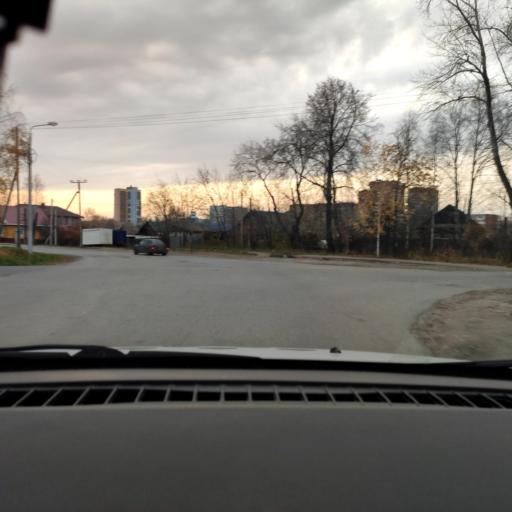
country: RU
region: Perm
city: Polazna
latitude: 58.1239
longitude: 56.3971
